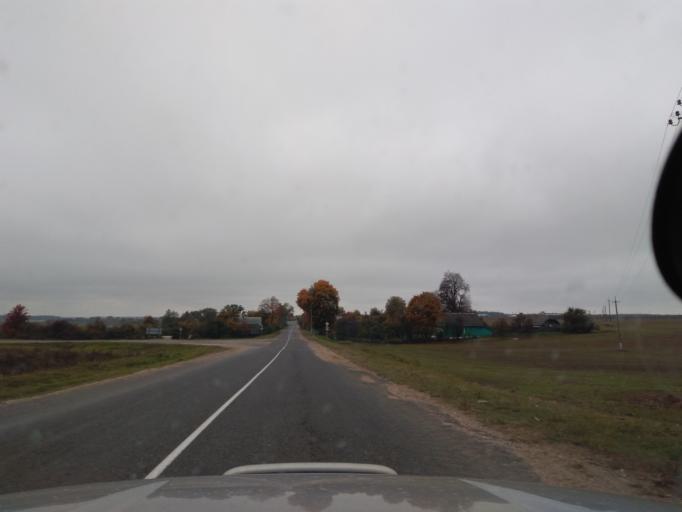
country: BY
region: Minsk
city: Kapyl'
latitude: 53.1528
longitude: 27.1568
